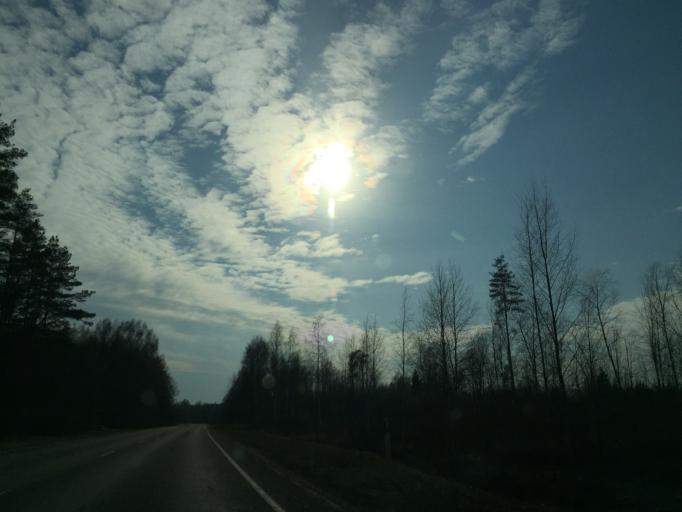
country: EE
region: Ida-Virumaa
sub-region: Kohtla-Nomme vald
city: Kohtla-Nomme
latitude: 59.0437
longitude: 27.2592
